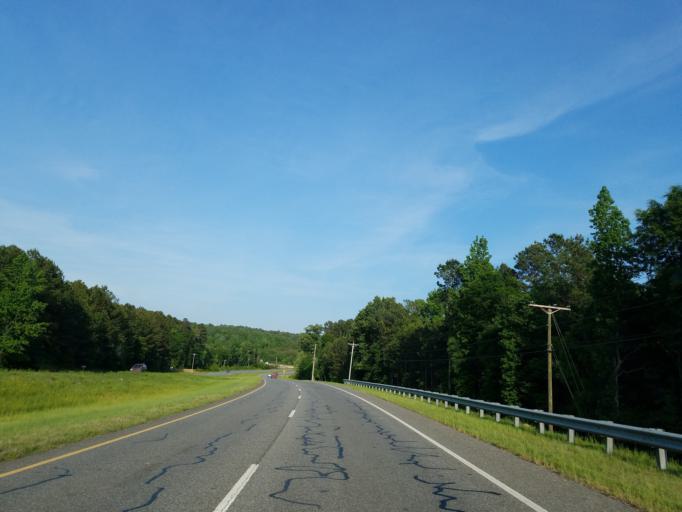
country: US
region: Georgia
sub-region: Chattooga County
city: Summerville
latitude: 34.4117
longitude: -85.2265
